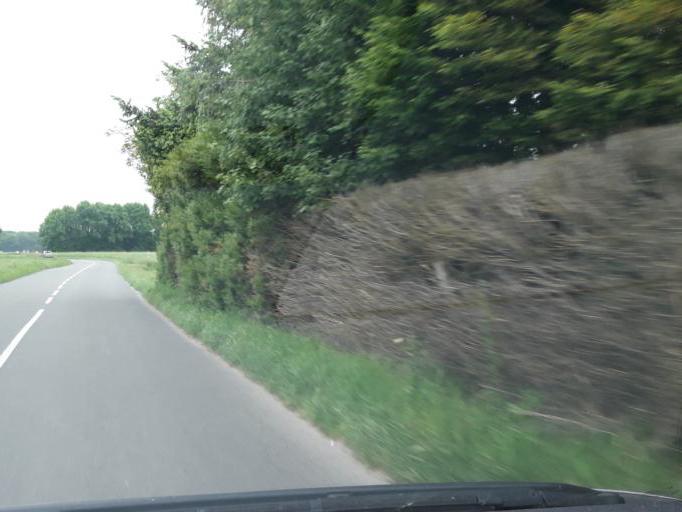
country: FR
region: Ile-de-France
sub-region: Departement de l'Essonne
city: Vert-le-Grand
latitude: 48.5827
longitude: 2.3639
